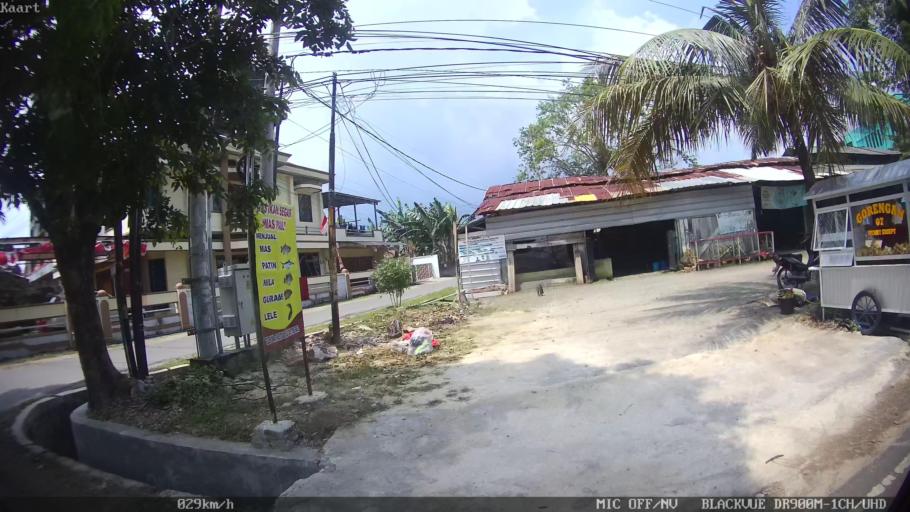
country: ID
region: Lampung
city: Kedaton
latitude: -5.4030
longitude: 105.2839
